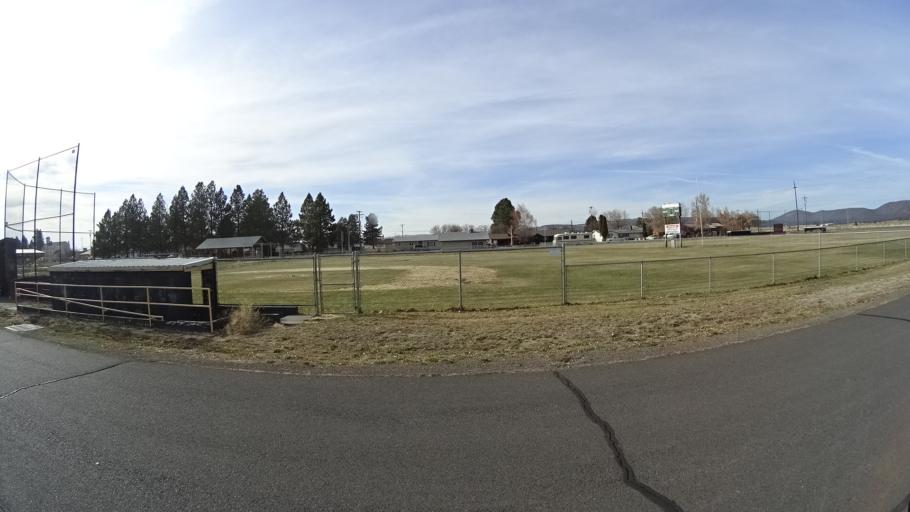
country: US
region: Oregon
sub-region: Klamath County
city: Klamath Falls
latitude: 41.9661
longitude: -121.9237
